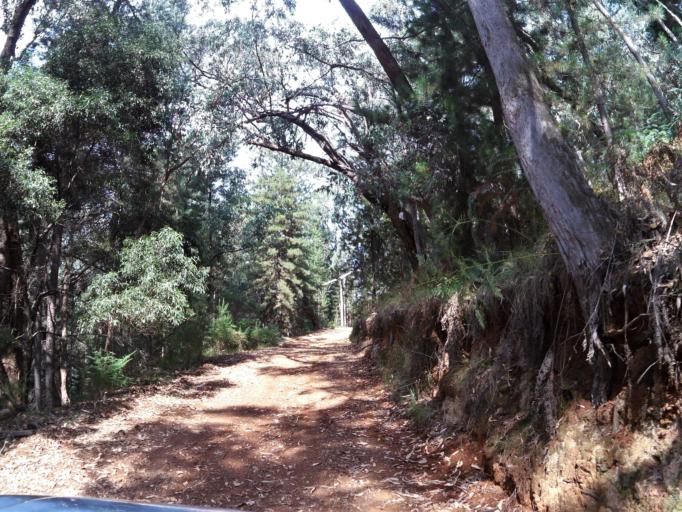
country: AU
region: Victoria
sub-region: Alpine
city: Mount Beauty
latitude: -36.7682
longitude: 147.0147
